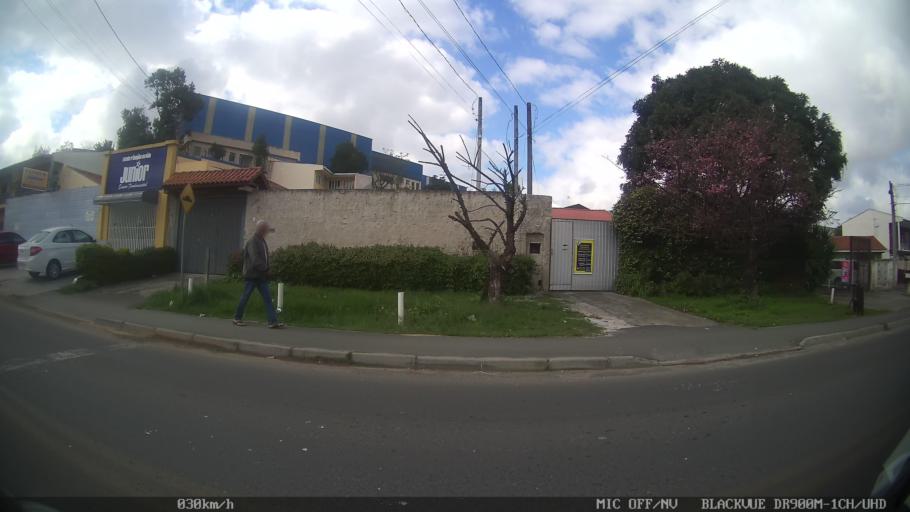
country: BR
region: Parana
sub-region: Colombo
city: Colombo
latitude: -25.3612
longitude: -49.2093
